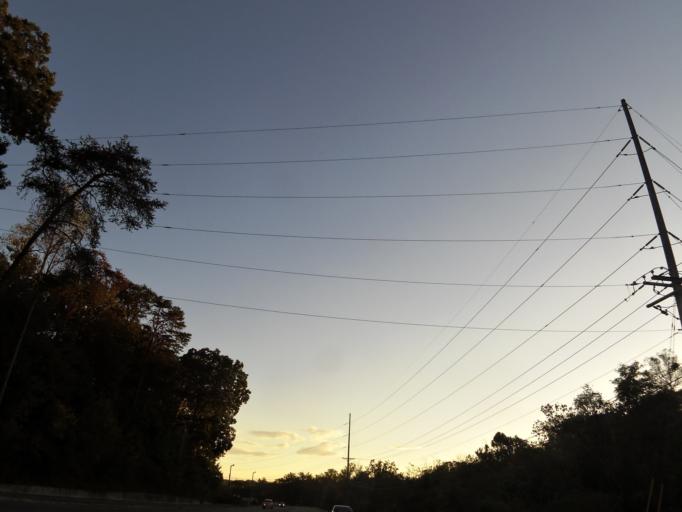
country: US
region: Tennessee
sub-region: Knox County
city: Farragut
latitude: 35.9354
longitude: -84.0613
